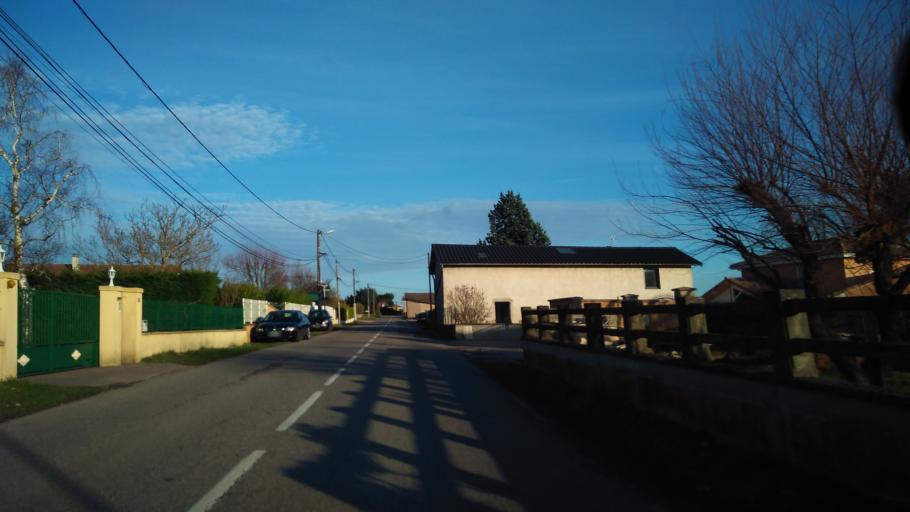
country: FR
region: Rhone-Alpes
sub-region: Departement de l'Isere
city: Valencin
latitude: 45.6061
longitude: 5.0409
